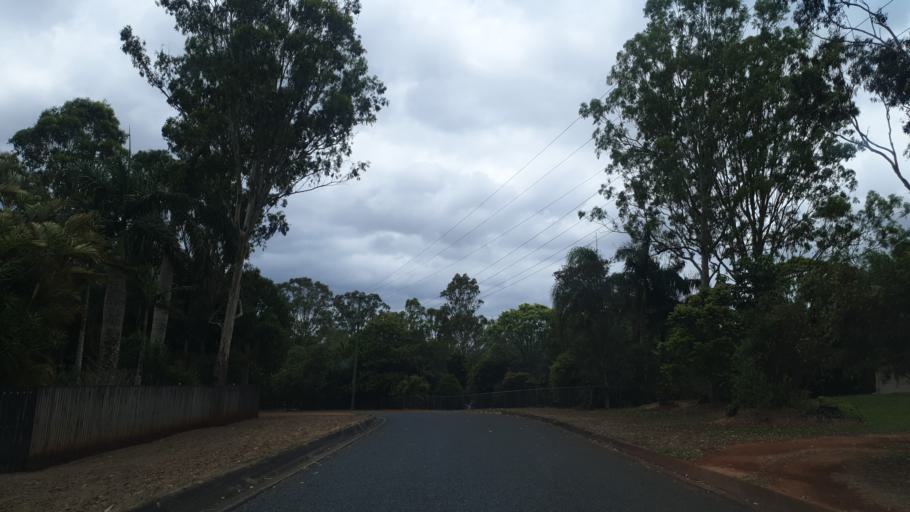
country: AU
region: Queensland
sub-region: Tablelands
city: Tolga
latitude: -17.2086
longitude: 145.4431
